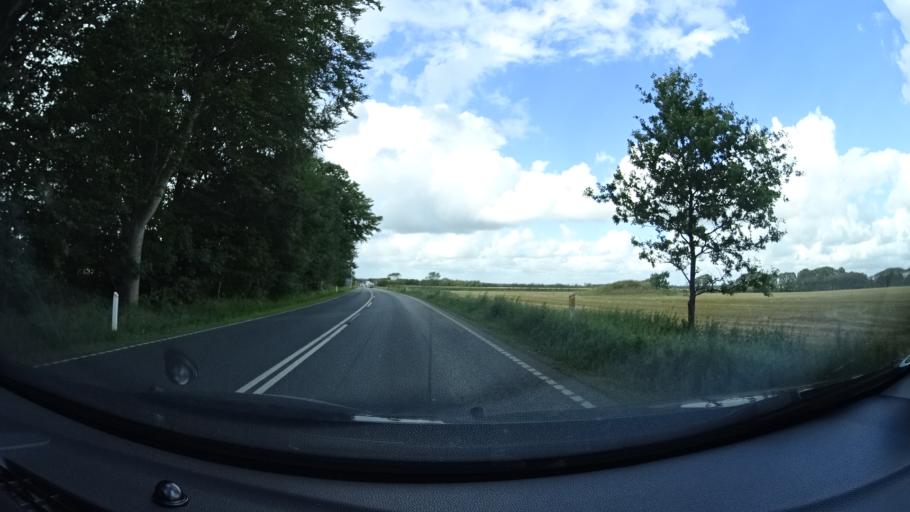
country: DK
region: South Denmark
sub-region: Esbjerg Kommune
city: Tjaereborg
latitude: 55.5471
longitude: 8.5715
